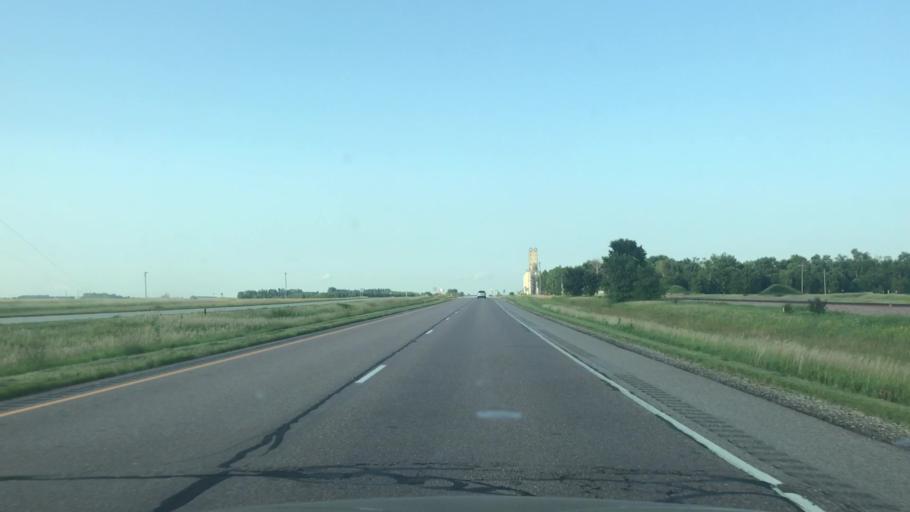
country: US
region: Minnesota
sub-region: Jackson County
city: Lakefield
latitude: 43.7617
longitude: -95.3742
